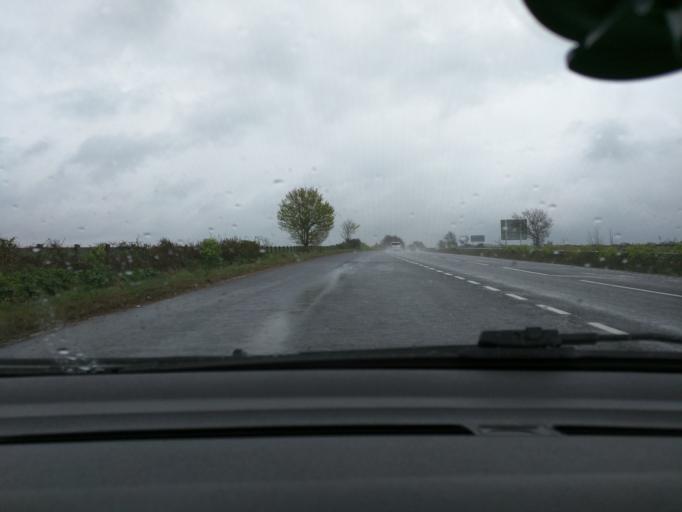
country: GB
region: England
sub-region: Suffolk
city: Wickham Market
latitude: 52.1637
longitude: 1.3856
